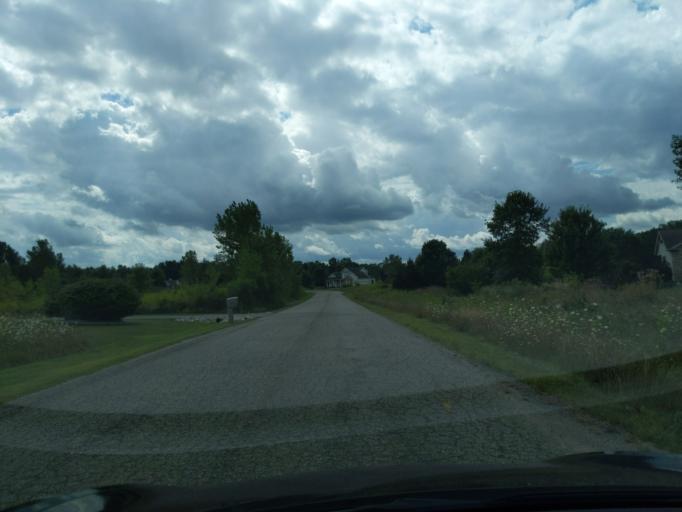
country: US
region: Michigan
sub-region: Eaton County
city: Dimondale
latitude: 42.5812
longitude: -84.5944
